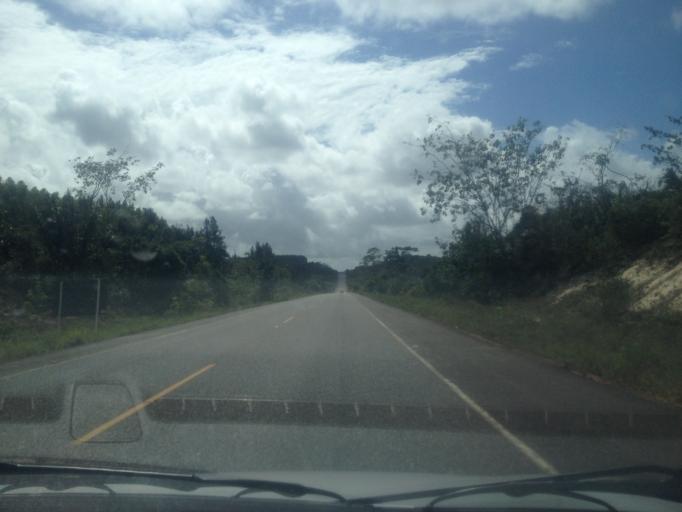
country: BR
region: Bahia
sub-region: Entre Rios
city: Entre Rios
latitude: -12.2305
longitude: -37.8401
